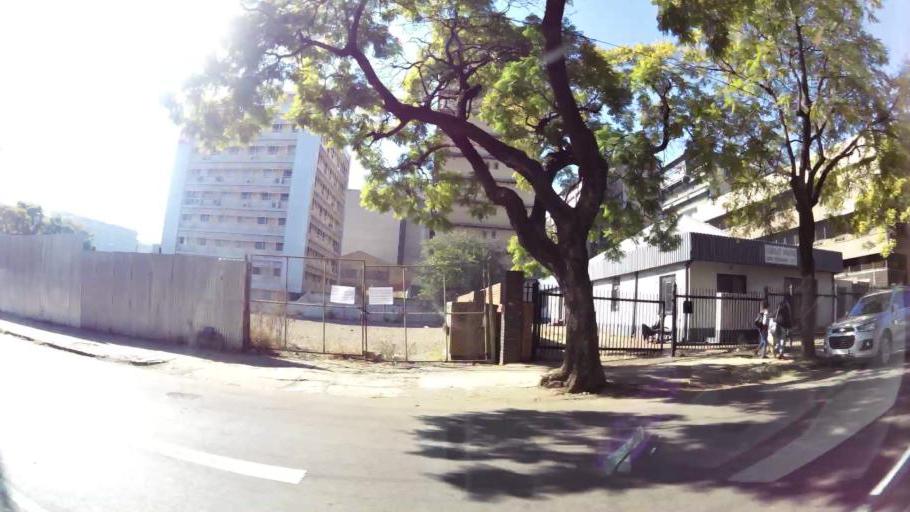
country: ZA
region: Gauteng
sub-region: City of Tshwane Metropolitan Municipality
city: Pretoria
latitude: -25.7515
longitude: 28.1861
